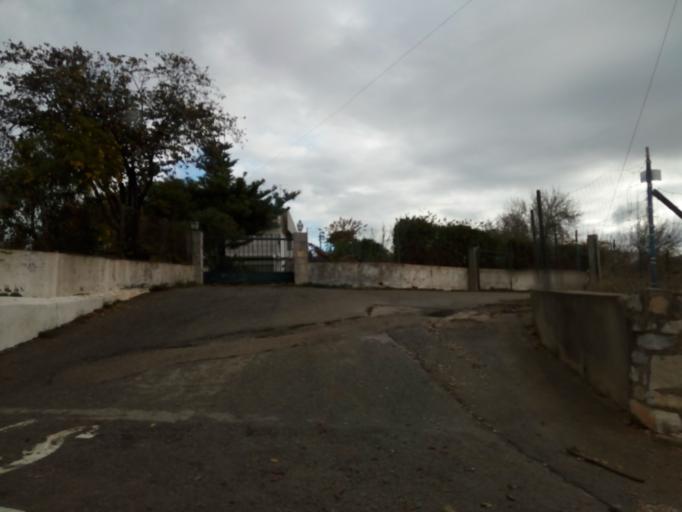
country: PT
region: Faro
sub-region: Loule
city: Loule
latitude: 37.1309
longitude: -8.0181
